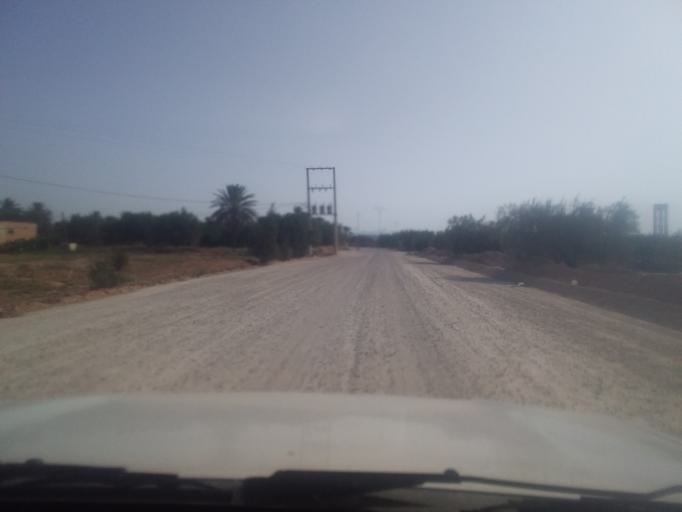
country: TN
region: Qabis
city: Matmata
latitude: 33.6020
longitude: 10.2767
